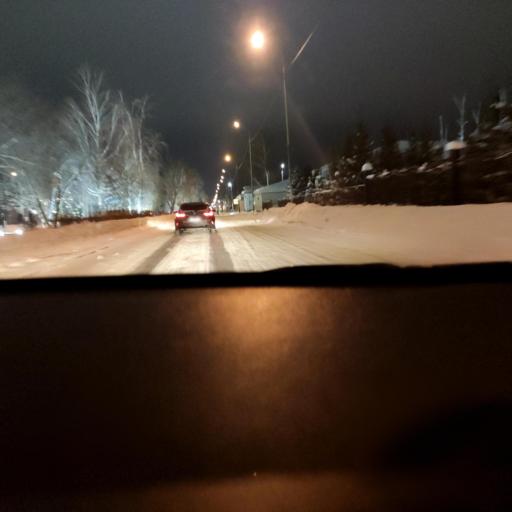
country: RU
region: Tatarstan
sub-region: Chistopol'skiy Rayon
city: Chistopol'
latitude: 55.3651
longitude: 50.6445
